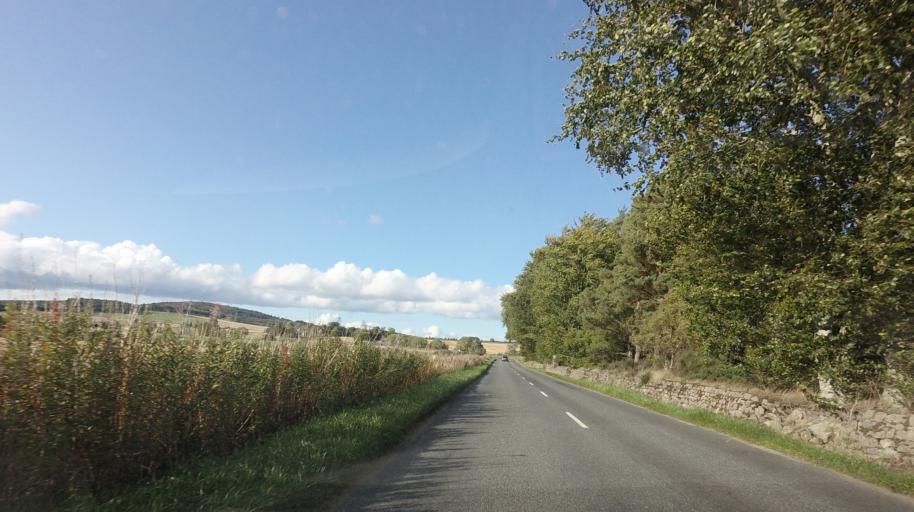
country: GB
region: Scotland
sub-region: Aberdeenshire
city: Banchory
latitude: 57.1318
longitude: -2.4278
